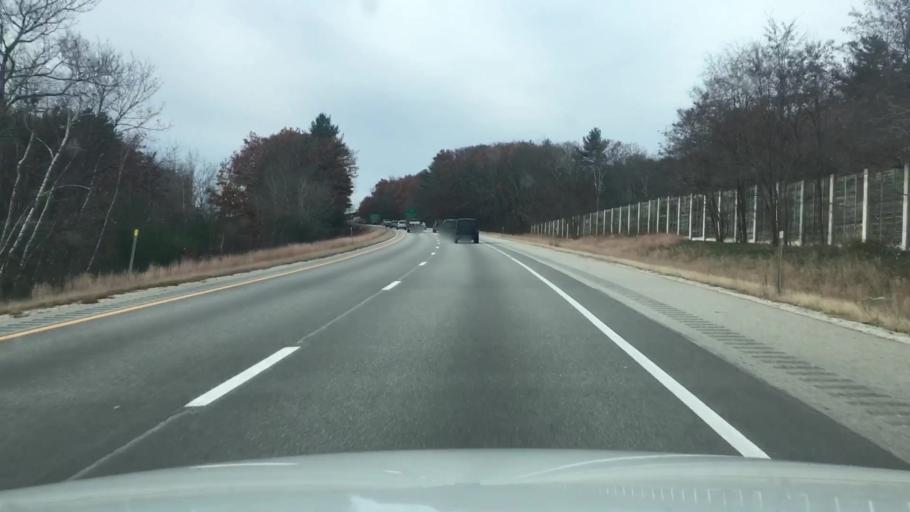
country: US
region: New Hampshire
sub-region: Merrimack County
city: South Hooksett
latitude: 43.0027
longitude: -71.4060
